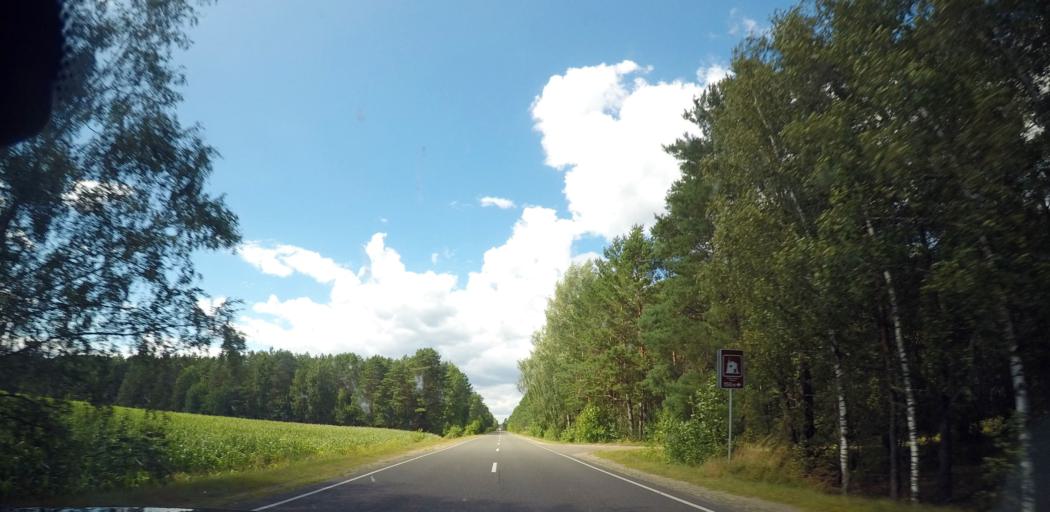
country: LT
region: Alytaus apskritis
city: Druskininkai
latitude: 53.8737
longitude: 24.1537
